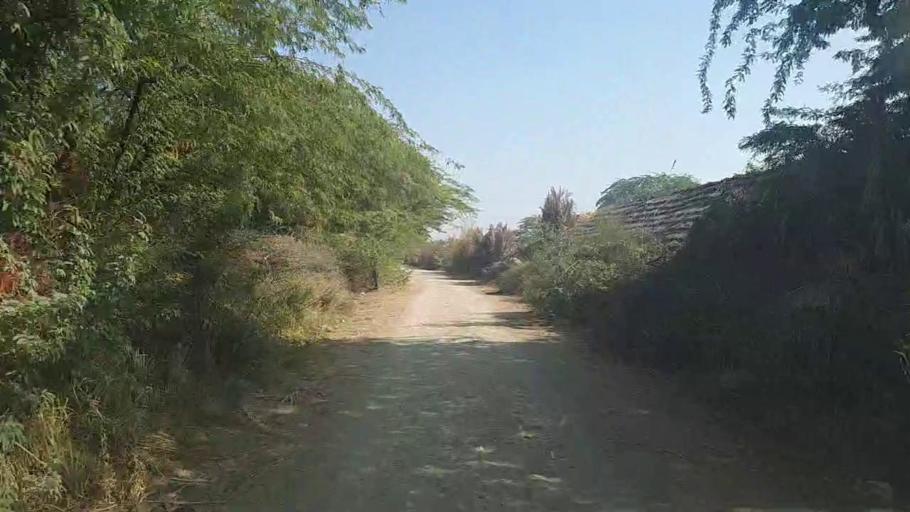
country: PK
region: Sindh
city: Kot Diji
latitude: 27.4315
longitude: 68.7231
